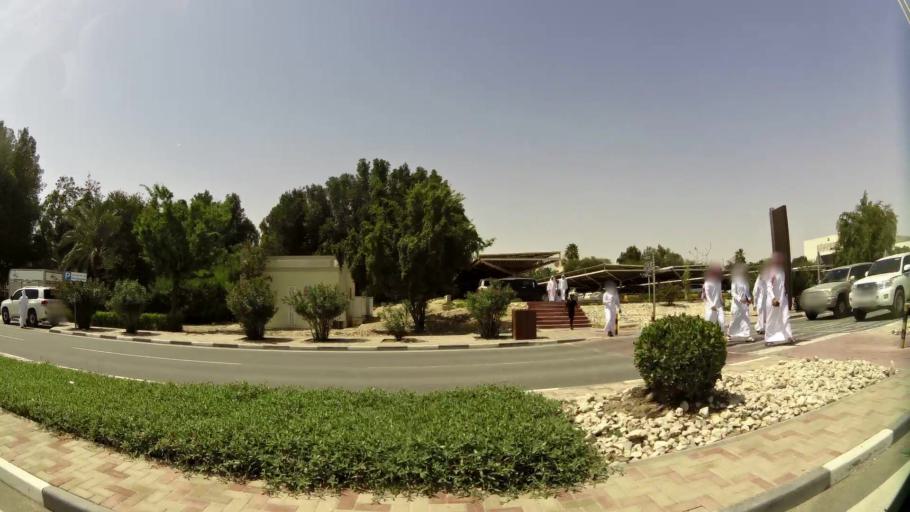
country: QA
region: Baladiyat Umm Salal
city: Umm Salal Muhammad
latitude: 25.3756
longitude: 51.4929
